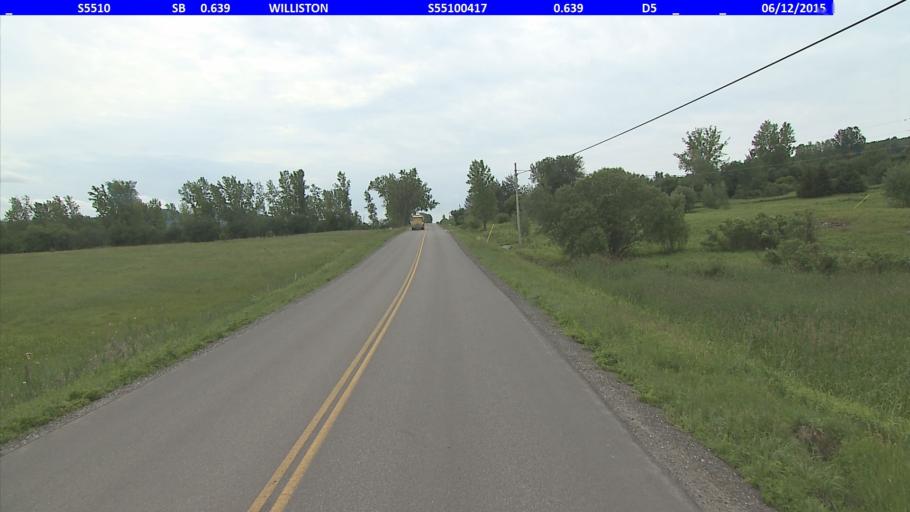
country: US
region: Vermont
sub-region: Chittenden County
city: Hinesburg
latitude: 44.3816
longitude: -73.0973
